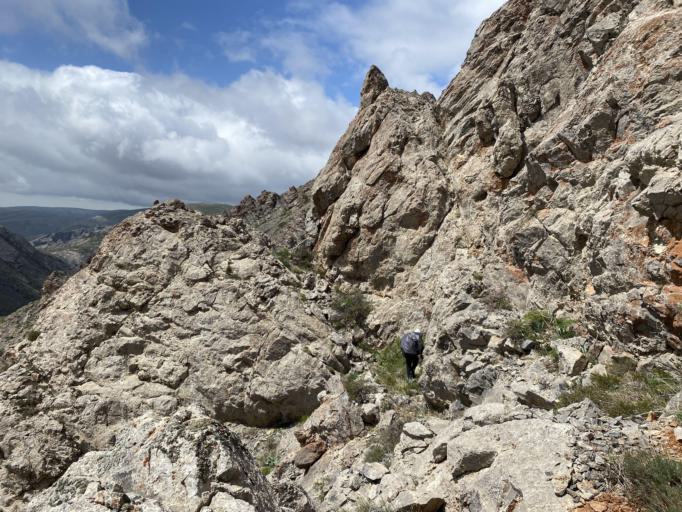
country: KZ
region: Ongtustik Qazaqstan
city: Ashchysay
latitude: 43.6396
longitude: 68.9260
